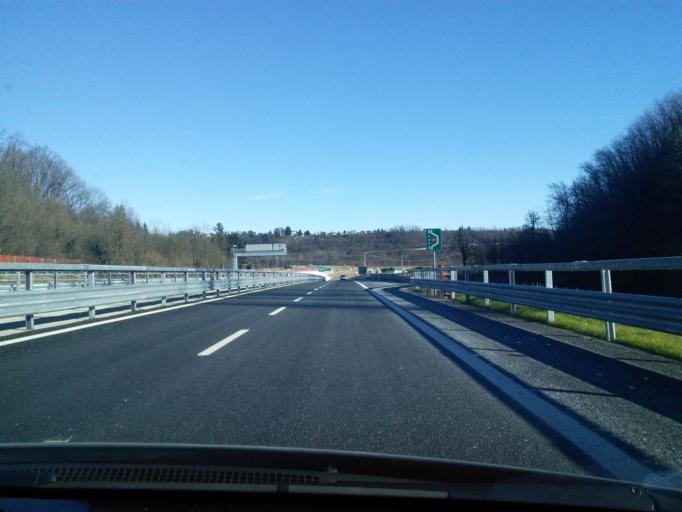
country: IT
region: Lombardy
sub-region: Provincia di Varese
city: Lozza
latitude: 45.7721
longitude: 8.8541
